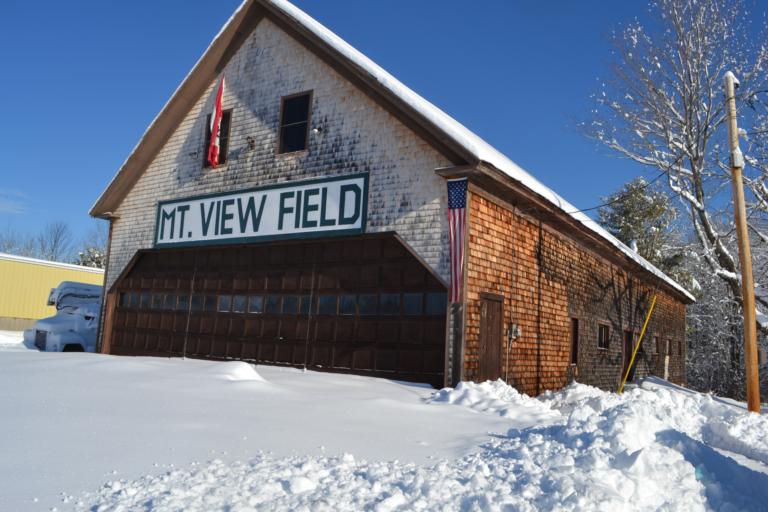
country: US
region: New Hampshire
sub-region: Carroll County
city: Ossipee
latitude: 43.6530
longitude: -71.1500
